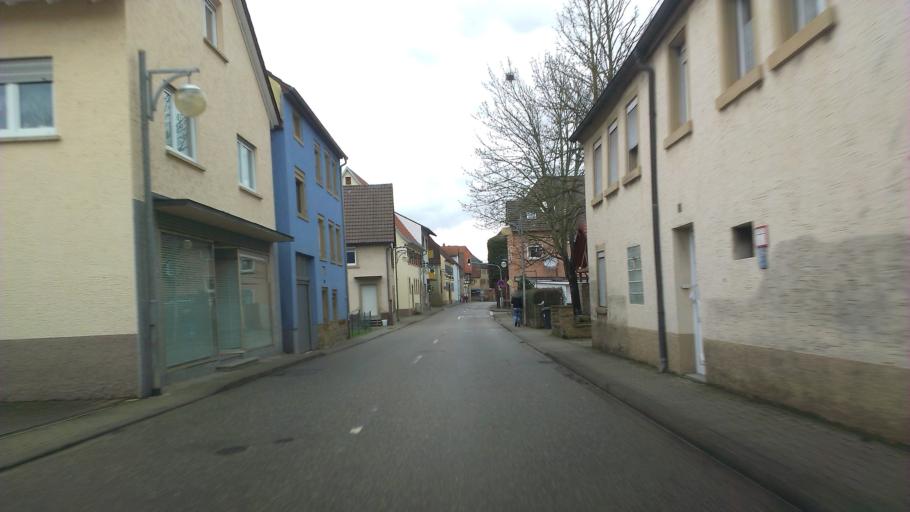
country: DE
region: Baden-Wuerttemberg
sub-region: Karlsruhe Region
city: Sulzfeld
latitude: 49.1012
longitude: 8.8568
